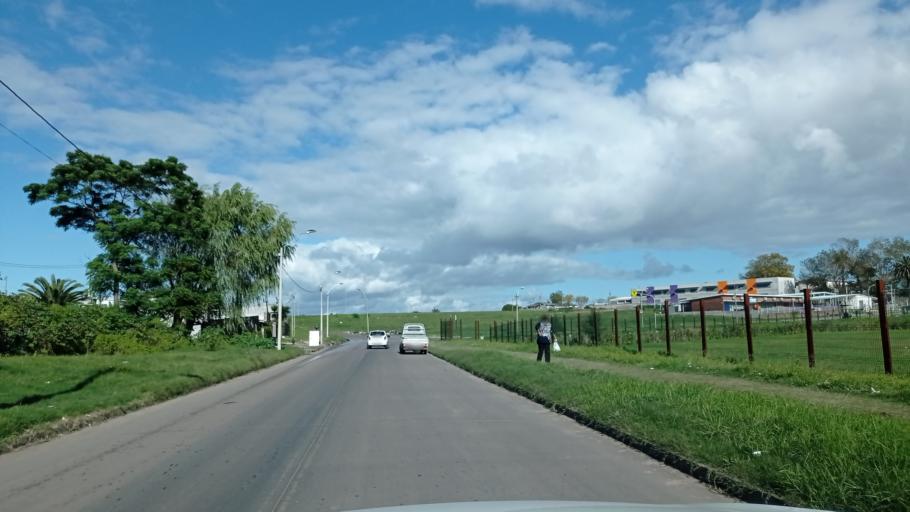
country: UY
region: Canelones
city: Paso de Carrasco
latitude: -34.8770
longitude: -56.1175
